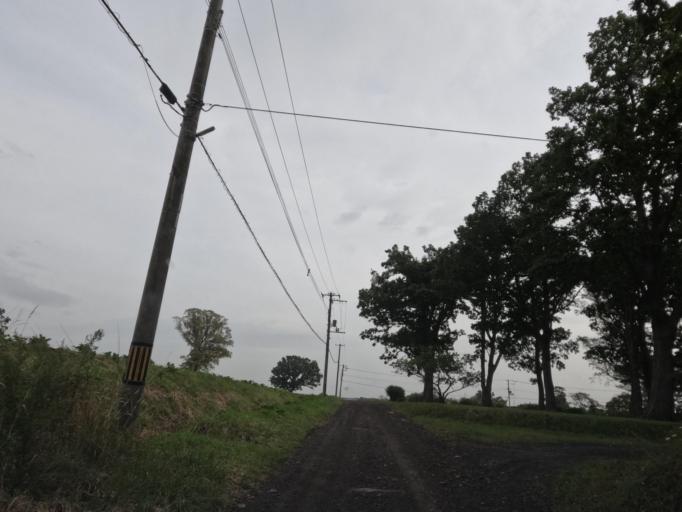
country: JP
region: Hokkaido
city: Date
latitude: 42.4255
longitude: 140.9161
